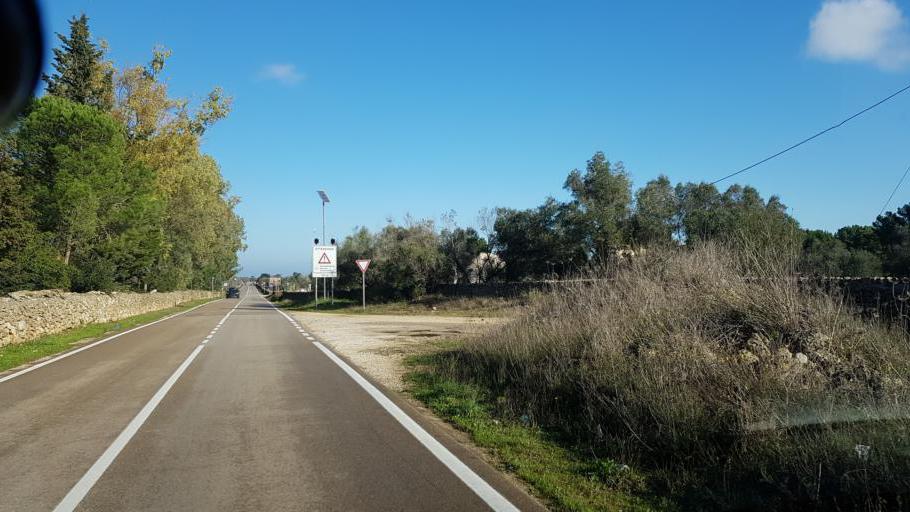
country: IT
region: Apulia
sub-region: Provincia di Lecce
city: Trepuzzi
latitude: 40.4576
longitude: 18.1140
